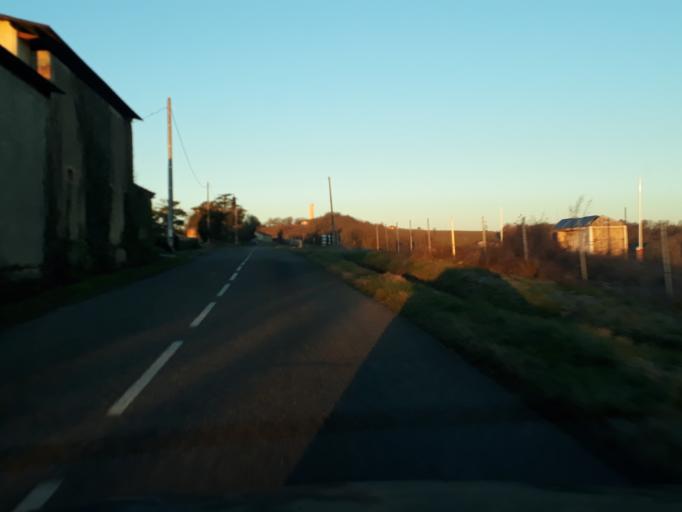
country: FR
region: Midi-Pyrenees
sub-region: Departement du Gers
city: Aubiet
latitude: 43.6006
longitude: 0.7086
